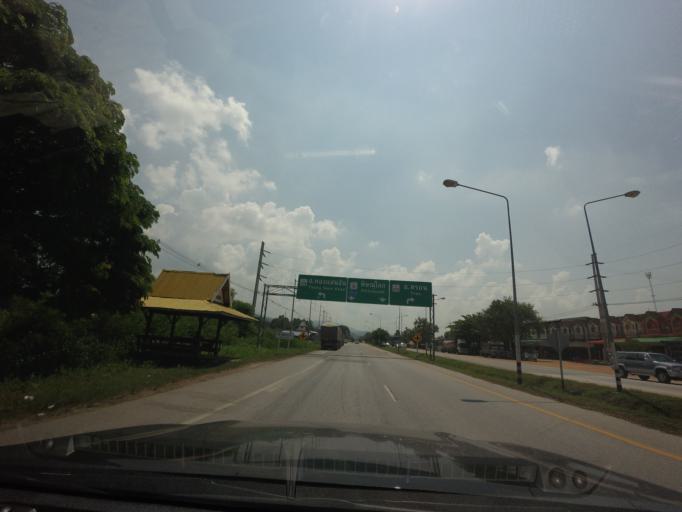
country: TH
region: Uttaradit
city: Thong Saen Khan
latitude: 17.4737
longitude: 100.2360
